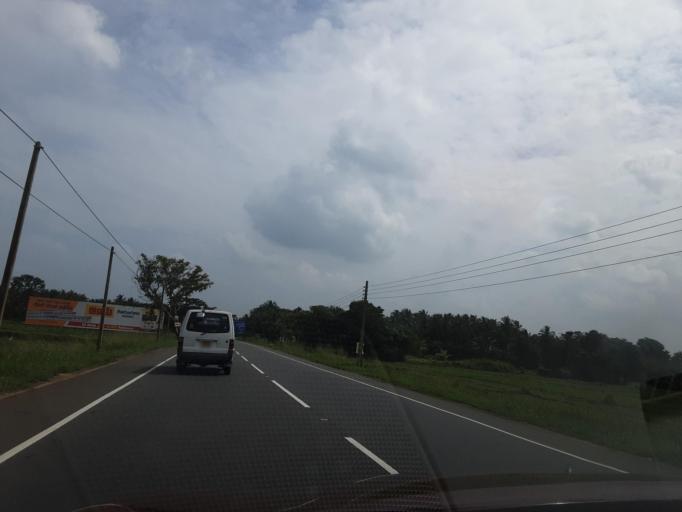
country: LK
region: North Central
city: Anuradhapura
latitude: 8.4794
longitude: 80.5111
